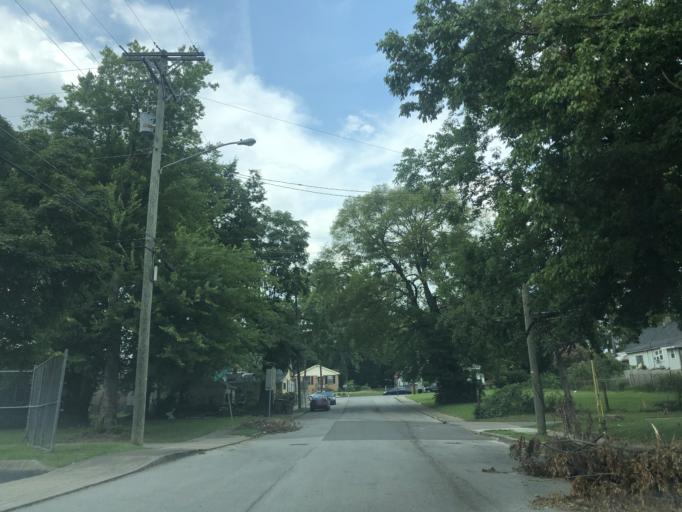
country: US
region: Tennessee
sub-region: Davidson County
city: Nashville
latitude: 36.1507
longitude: -86.7552
